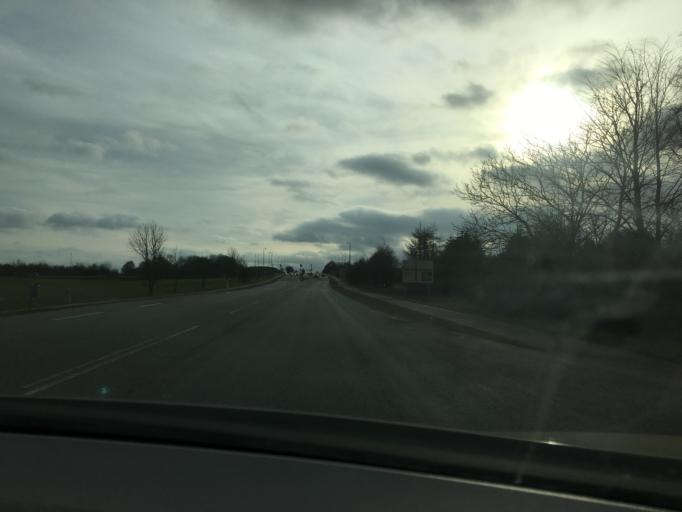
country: DK
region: Central Jutland
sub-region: Hedensted Kommune
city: Hedensted
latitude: 55.7409
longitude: 9.6261
